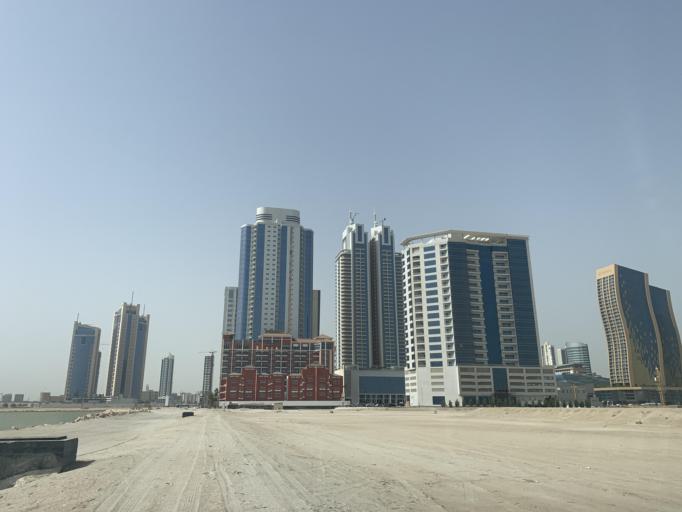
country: BH
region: Manama
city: Jidd Hafs
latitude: 26.2398
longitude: 50.5571
